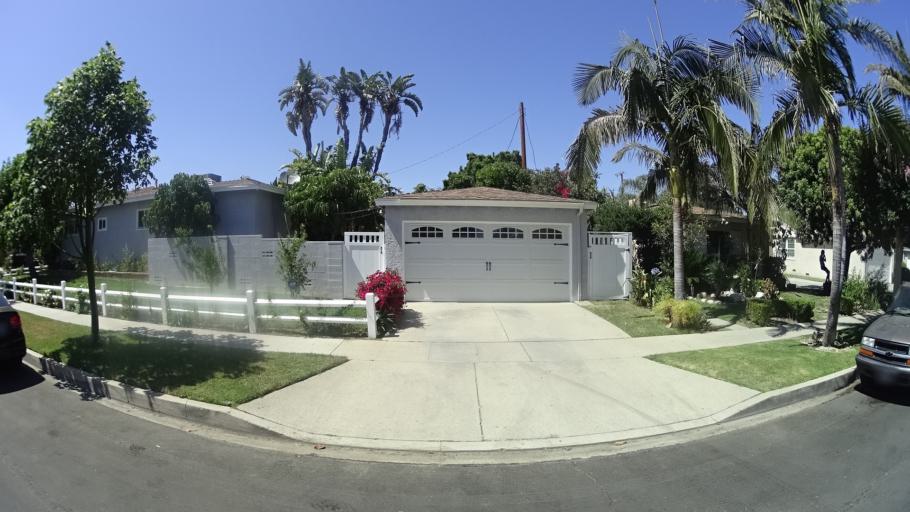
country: US
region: California
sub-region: Los Angeles County
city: Van Nuys
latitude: 34.1876
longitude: -118.4966
